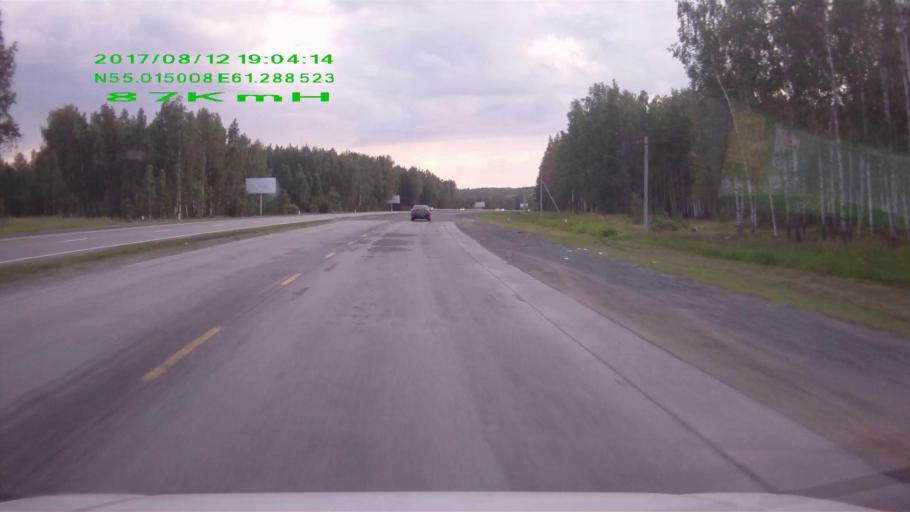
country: RU
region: Chelyabinsk
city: Sargazy
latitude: 55.0117
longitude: 61.2721
